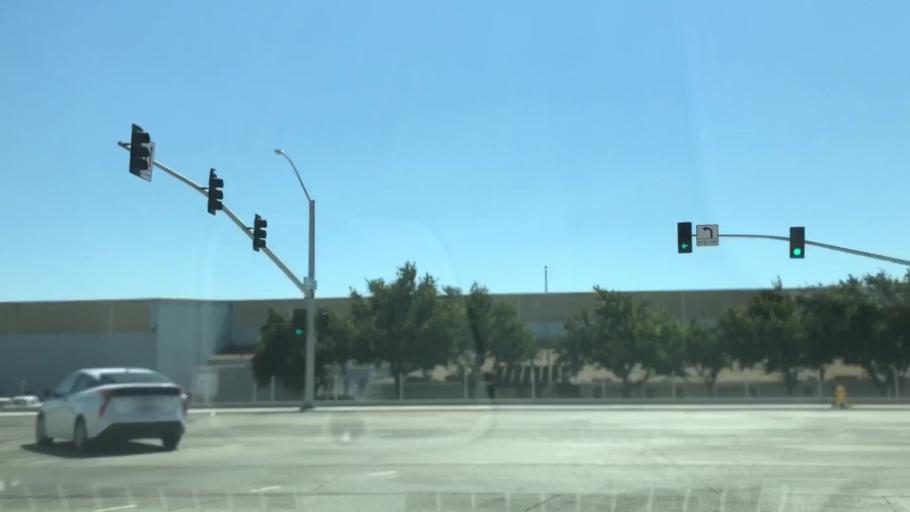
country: US
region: California
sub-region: San Joaquin County
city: Country Club
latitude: 37.9377
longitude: -121.3228
